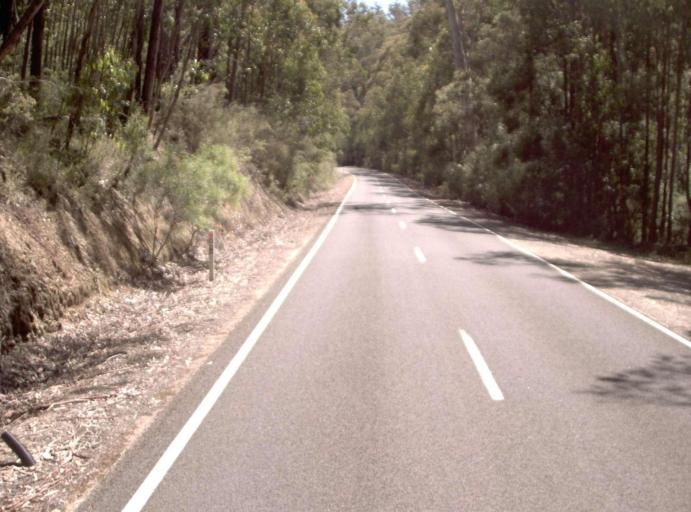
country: AU
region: Victoria
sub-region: East Gippsland
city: Lakes Entrance
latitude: -37.3653
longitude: 148.2191
